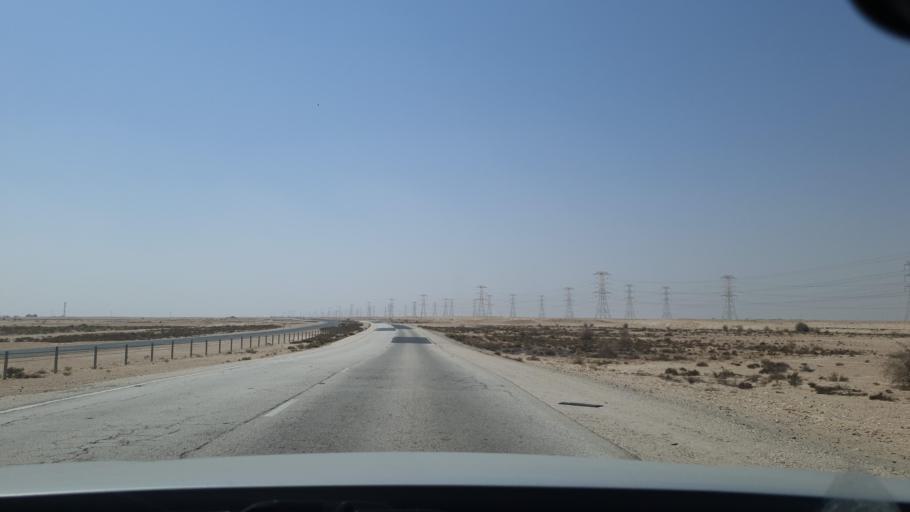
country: QA
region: Al Khawr
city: Al Khawr
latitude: 25.7452
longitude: 51.4640
